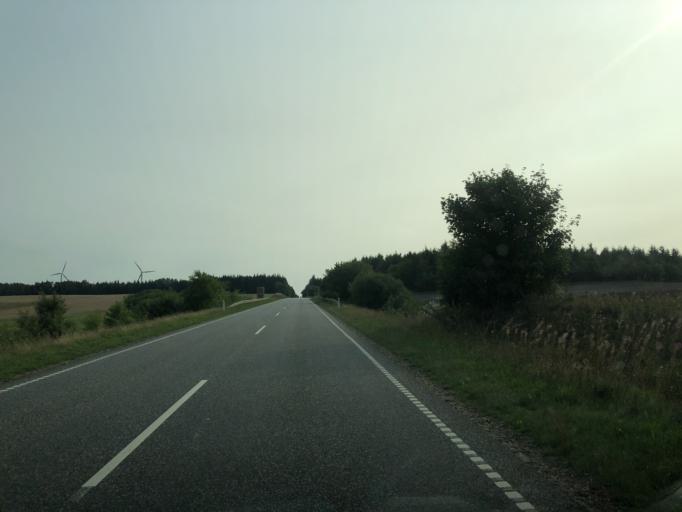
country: DK
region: Central Jutland
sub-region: Herning Kommune
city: Vildbjerg
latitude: 56.1816
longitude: 8.7004
